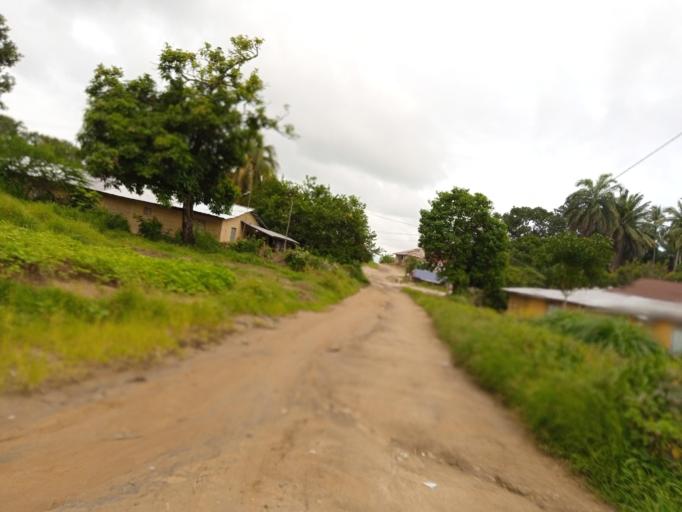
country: SL
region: Northern Province
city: Masoyila
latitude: 8.5955
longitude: -13.2008
